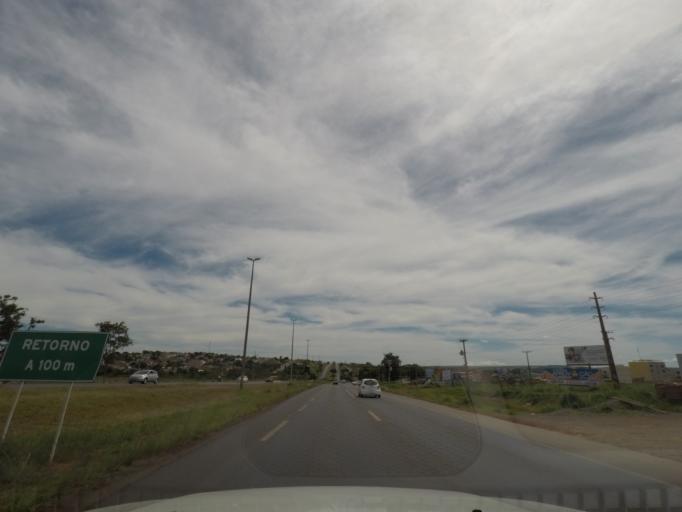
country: BR
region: Goias
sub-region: Planaltina
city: Planaltina
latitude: -15.6091
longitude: -47.6955
